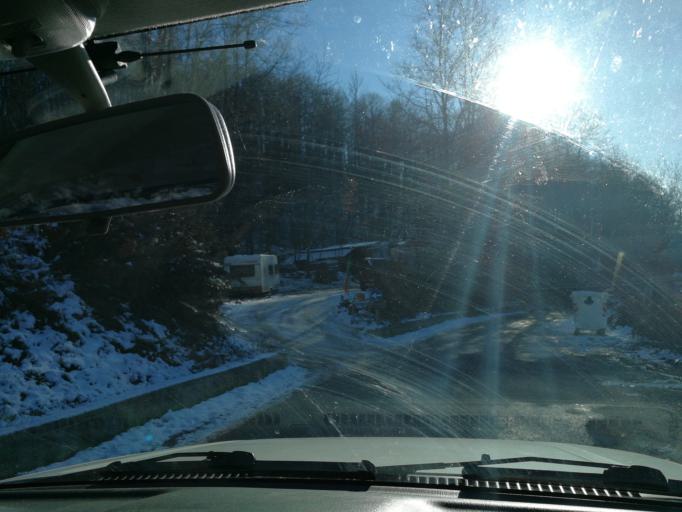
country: IT
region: Latium
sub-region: Provincia di Rieti
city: Amatrice
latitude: 42.6724
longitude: 13.2939
